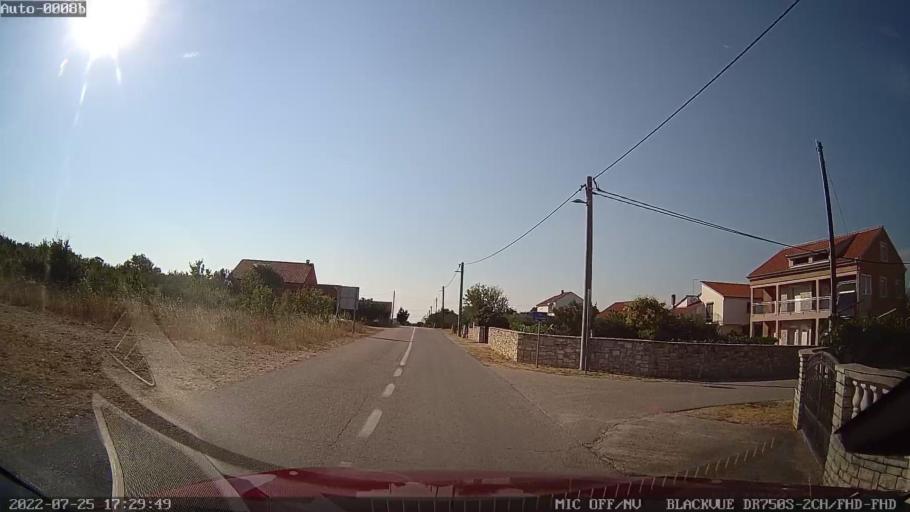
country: HR
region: Zadarska
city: Pridraga
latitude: 44.1612
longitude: 15.5141
